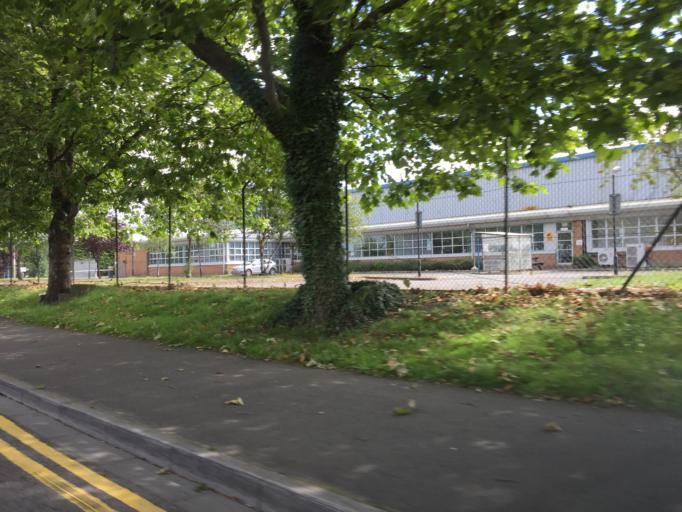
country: GB
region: Wales
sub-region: Newport
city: Nash
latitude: 51.5701
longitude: -2.9655
